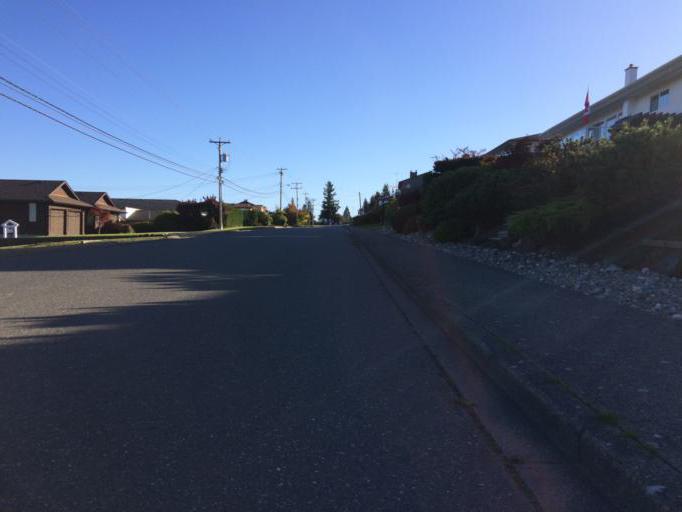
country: CA
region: British Columbia
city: Campbell River
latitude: 49.9988
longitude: -125.2353
